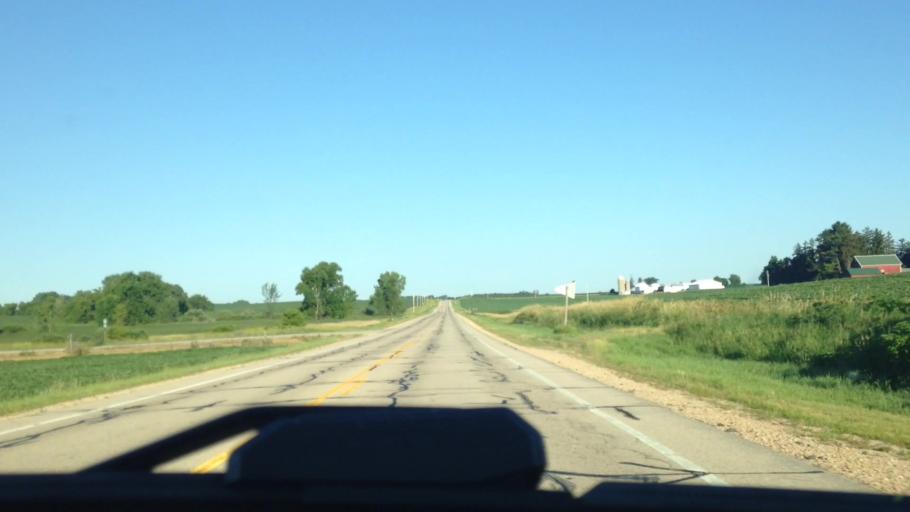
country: US
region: Wisconsin
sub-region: Columbia County
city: Rio
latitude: 43.3408
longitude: -89.2303
